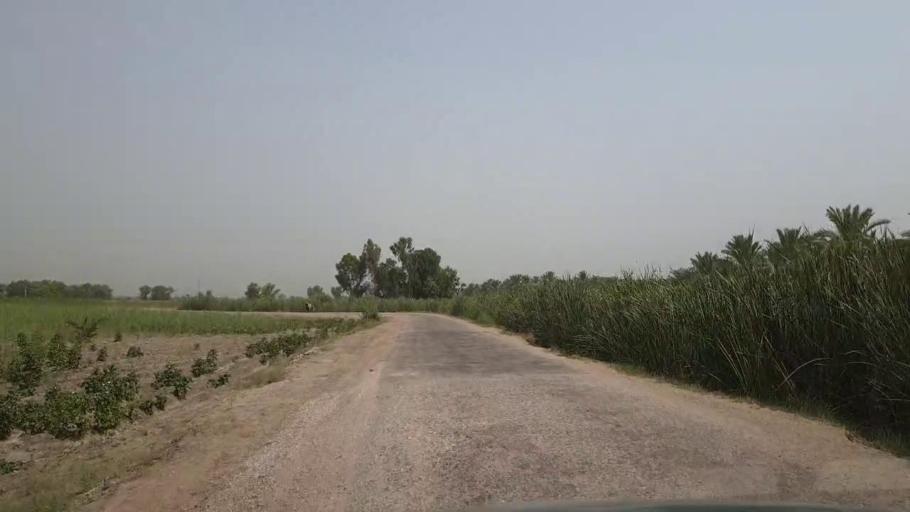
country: PK
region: Sindh
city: Gambat
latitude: 27.4034
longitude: 68.5509
